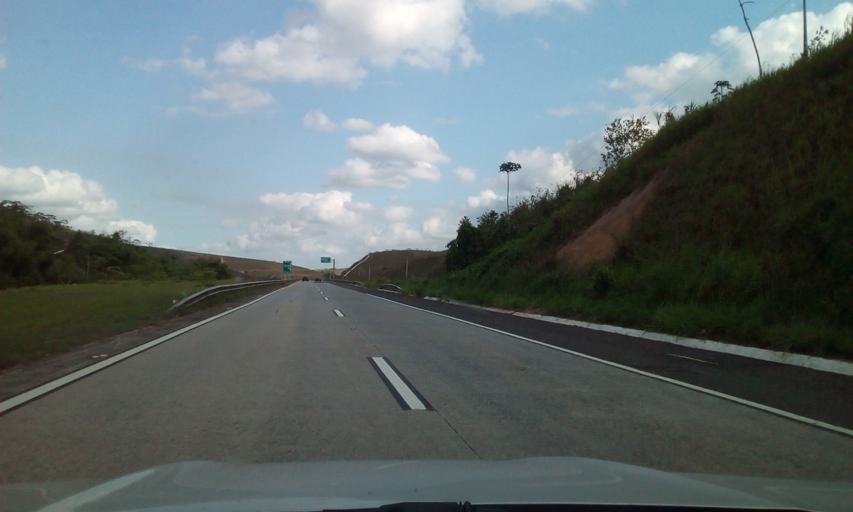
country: BR
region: Pernambuco
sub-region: Gameleira
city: Gameleira
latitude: -8.5518
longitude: -35.4384
